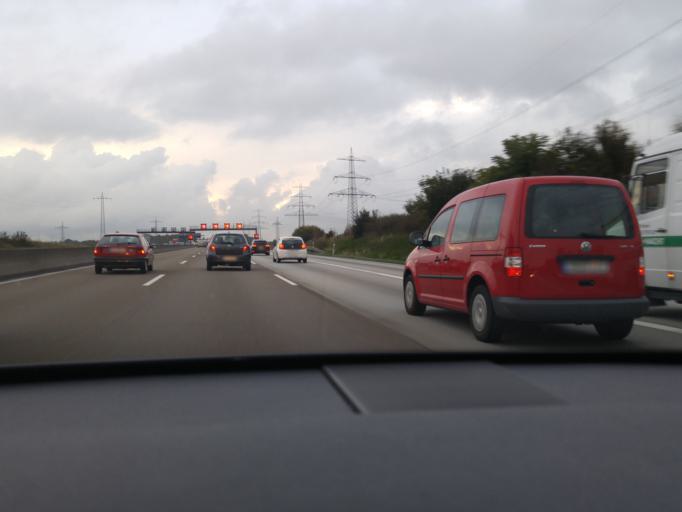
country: DE
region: Hesse
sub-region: Regierungsbezirk Darmstadt
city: Eschborn
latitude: 50.1442
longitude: 8.5962
